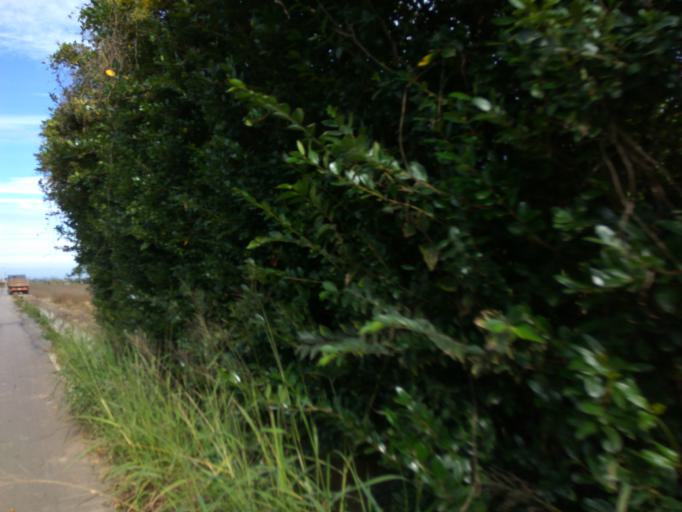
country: TW
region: Taiwan
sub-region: Hsinchu
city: Zhubei
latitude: 25.0076
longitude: 121.0747
